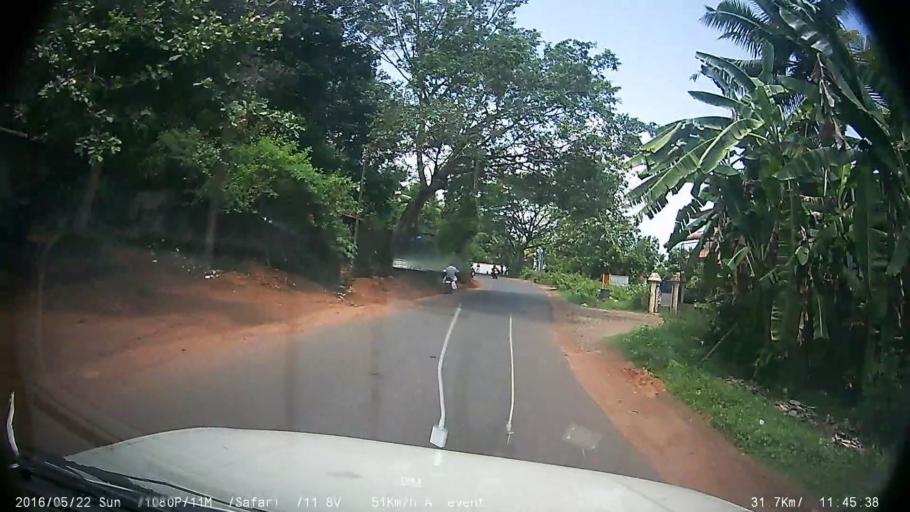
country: IN
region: Kerala
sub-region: Kottayam
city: Kottayam
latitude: 9.5388
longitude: 76.5212
